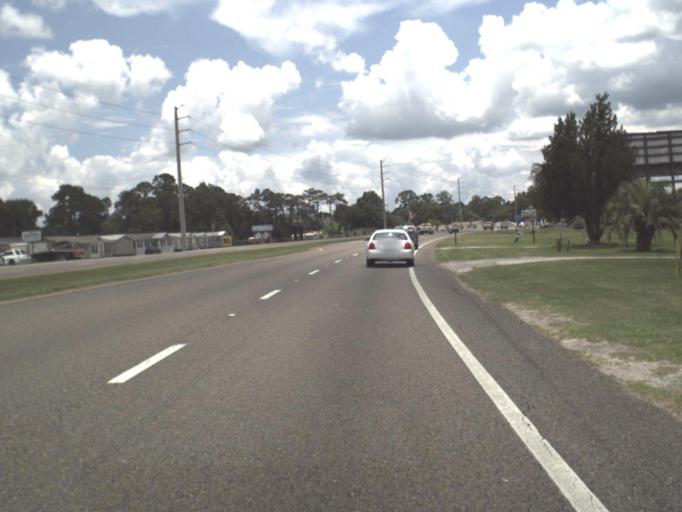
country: US
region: Florida
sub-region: Putnam County
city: East Palatka
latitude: 29.6416
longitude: -81.5911
